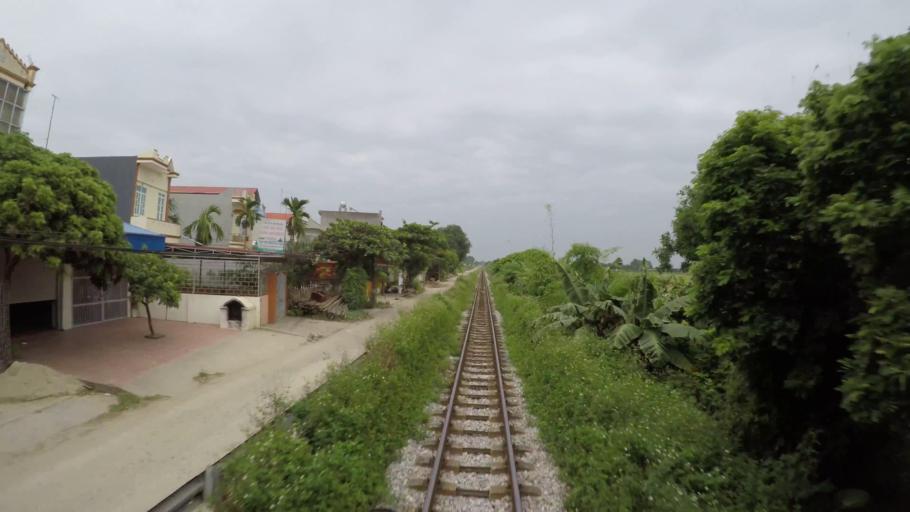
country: VN
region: Hai Duong
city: Lai Cach
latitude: 20.9516
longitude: 106.2359
